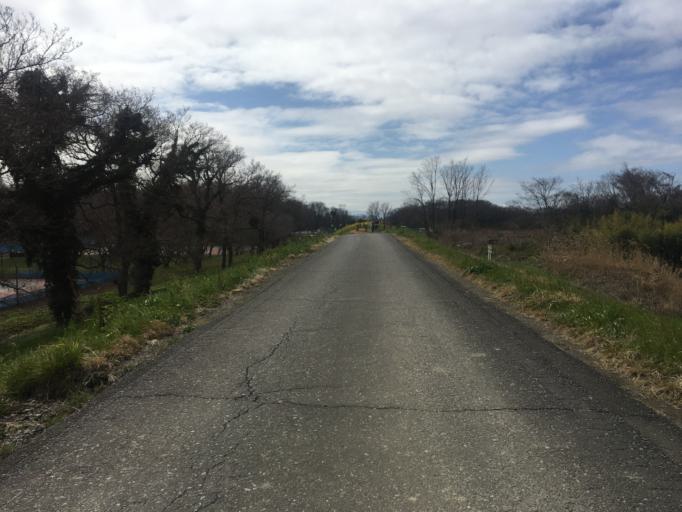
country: JP
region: Saitama
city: Shiki
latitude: 35.8520
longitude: 139.6081
